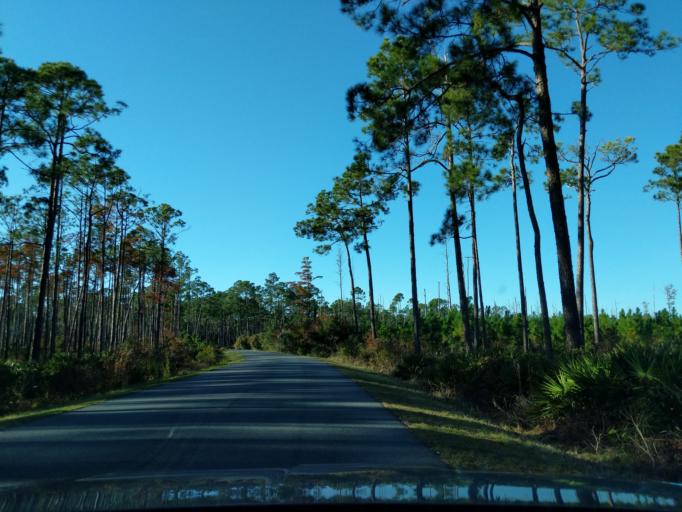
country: US
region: Georgia
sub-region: Charlton County
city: Folkston
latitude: 30.7106
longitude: -82.1524
